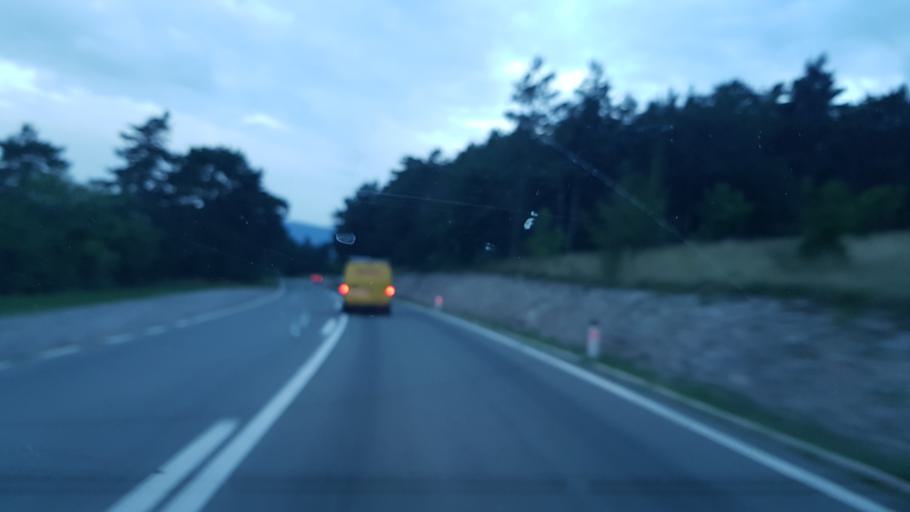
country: SI
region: Divaca
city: Divaca
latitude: 45.6980
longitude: 13.9857
